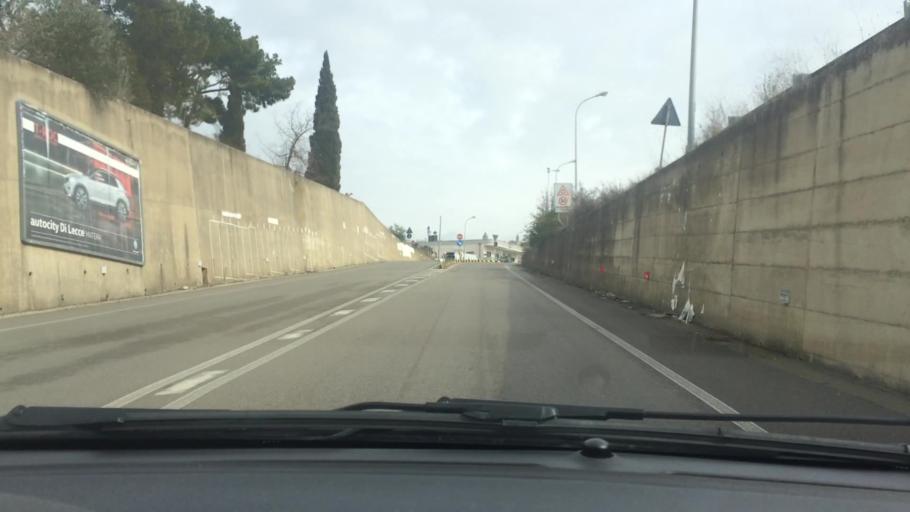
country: IT
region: Basilicate
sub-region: Provincia di Matera
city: Montescaglioso
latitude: 40.5497
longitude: 16.6566
